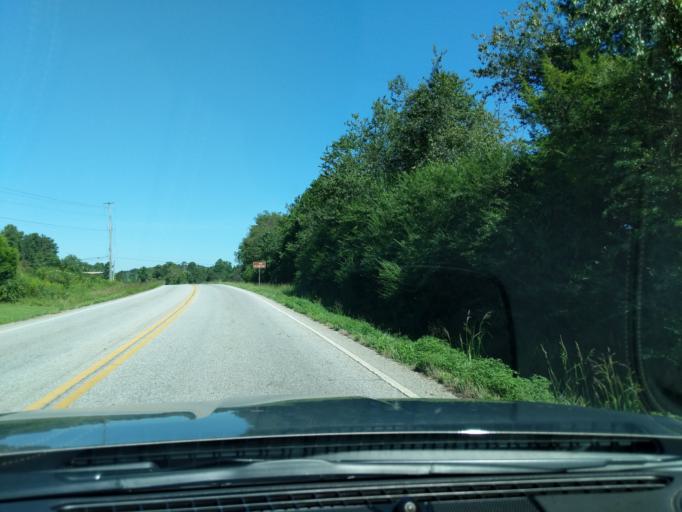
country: US
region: Georgia
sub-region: Habersham County
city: Demorest
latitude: 34.5612
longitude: -83.5764
